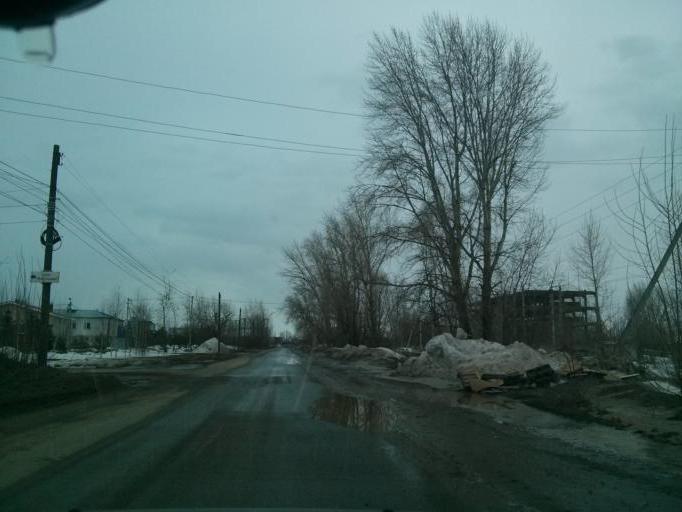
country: RU
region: Nizjnij Novgorod
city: Afonino
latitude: 56.2906
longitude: 44.1139
